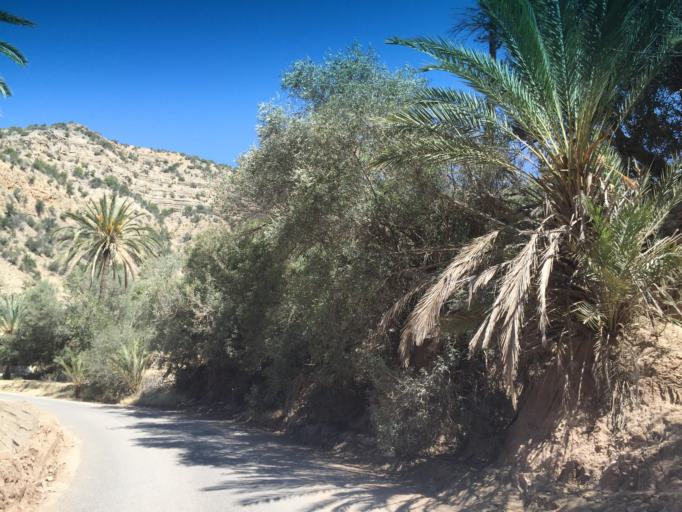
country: MA
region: Souss-Massa-Draa
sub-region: Agadir-Ida-ou-Tnan
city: Aourir
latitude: 30.5597
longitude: -9.5455
